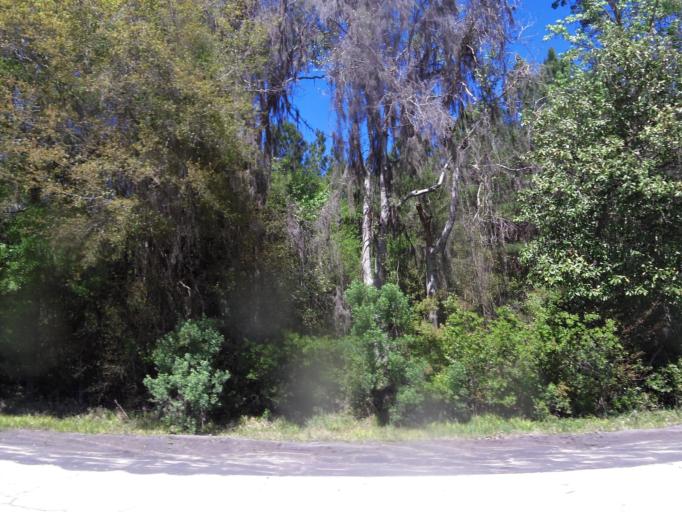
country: US
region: Florida
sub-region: Bradford County
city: Starke
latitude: 30.0559
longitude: -82.0507
